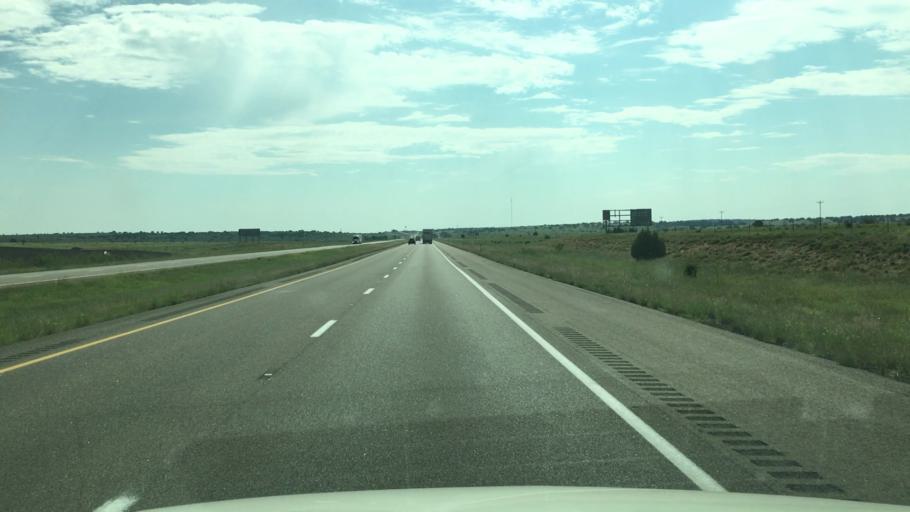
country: US
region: New Mexico
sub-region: Guadalupe County
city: Santa Rosa
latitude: 34.9891
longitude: -105.2486
